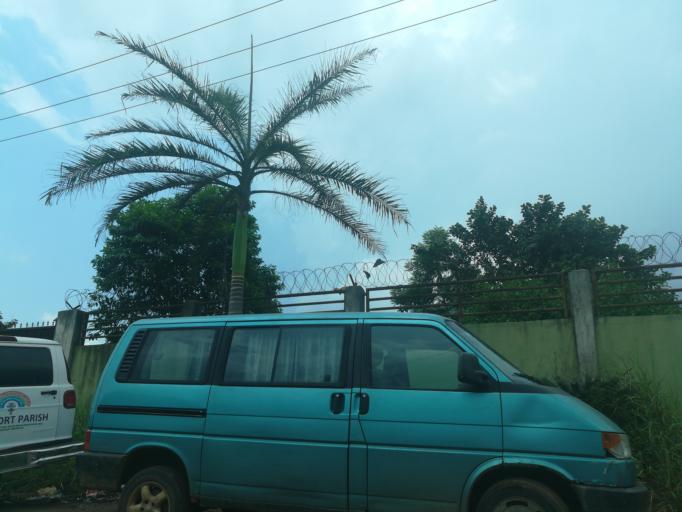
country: NG
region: Lagos
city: Ikorodu
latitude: 6.6708
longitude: 3.6705
